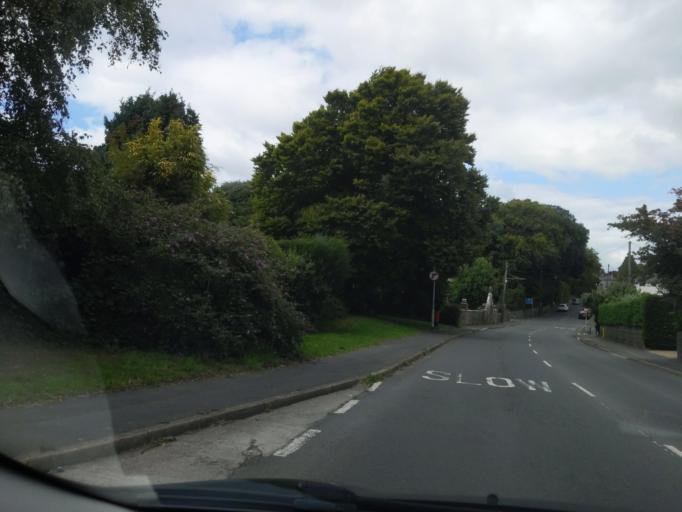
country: GB
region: England
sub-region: Plymouth
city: Plymstock
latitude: 50.3554
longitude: -4.0731
